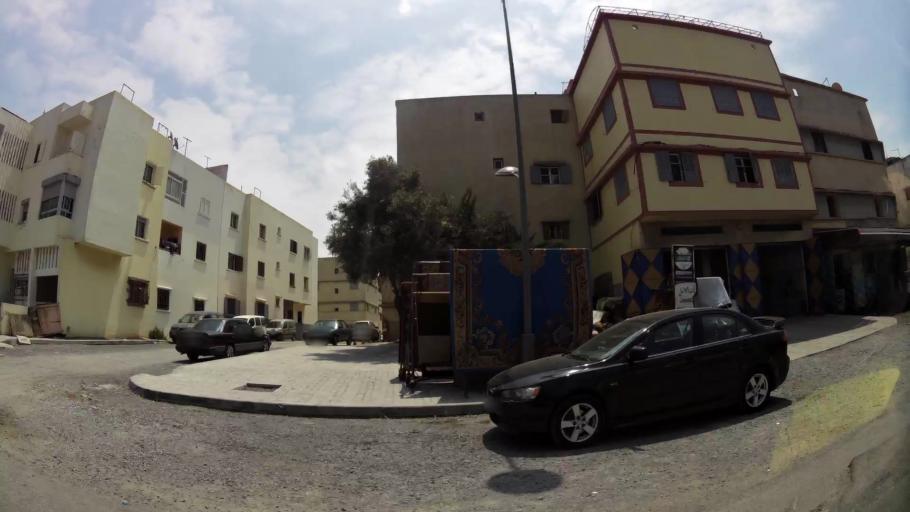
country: MA
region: Rabat-Sale-Zemmour-Zaer
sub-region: Skhirate-Temara
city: Temara
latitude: 33.9834
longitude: -6.8855
